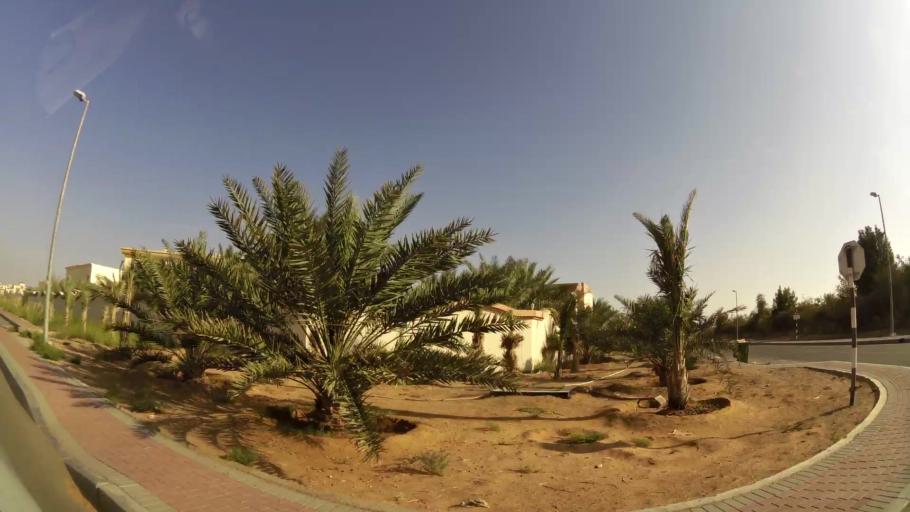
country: AE
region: Abu Dhabi
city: Al Ain
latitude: 24.0511
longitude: 55.8417
